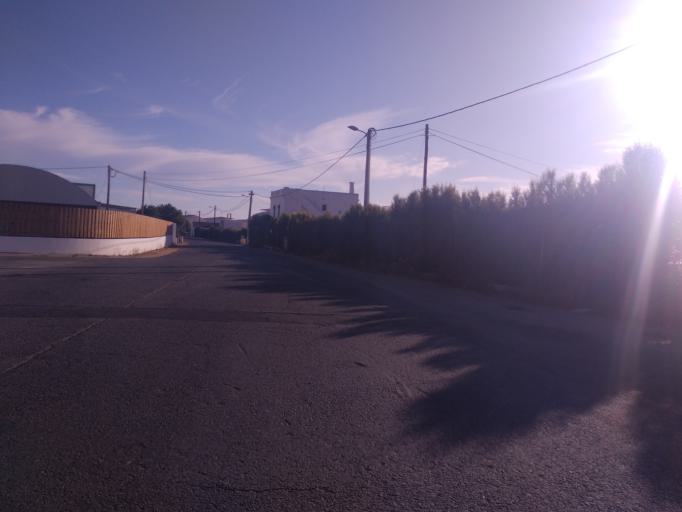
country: PT
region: Faro
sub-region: Faro
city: Faro
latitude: 37.0403
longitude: -7.9393
